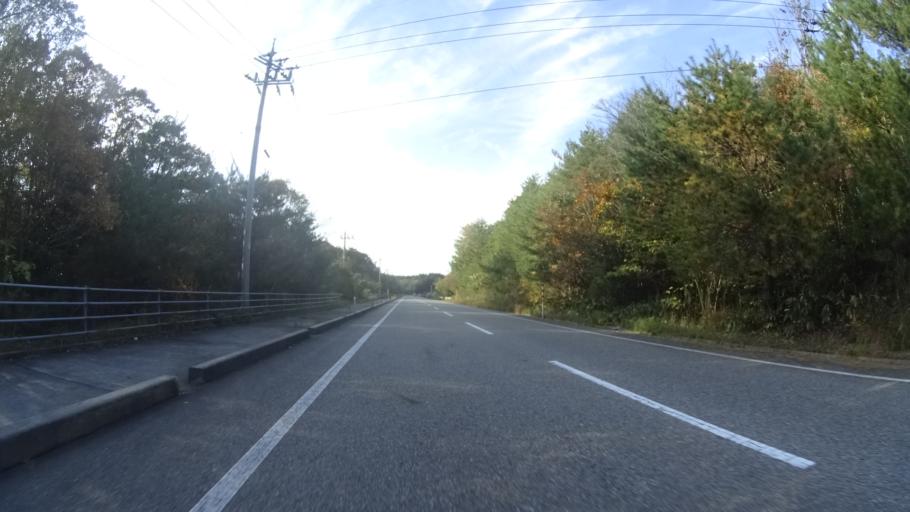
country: JP
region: Ishikawa
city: Hakui
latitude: 37.0722
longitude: 136.7347
